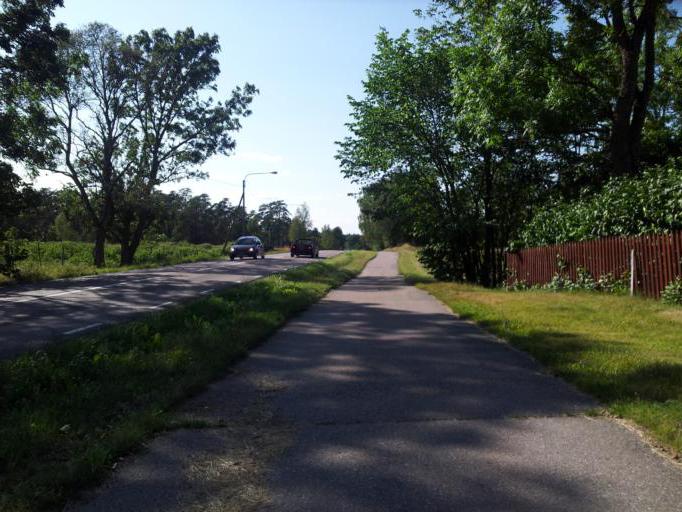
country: SE
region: Stockholm
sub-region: Norrtalje Kommun
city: Nykvarn
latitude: 59.8728
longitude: 18.0584
